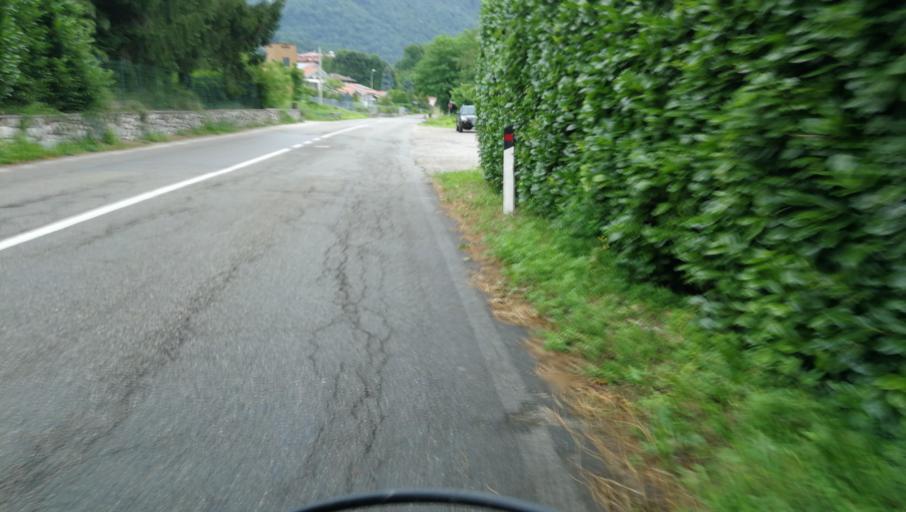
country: IT
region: Lombardy
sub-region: Provincia di Varese
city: Casalzuigno
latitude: 45.8997
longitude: 8.7043
